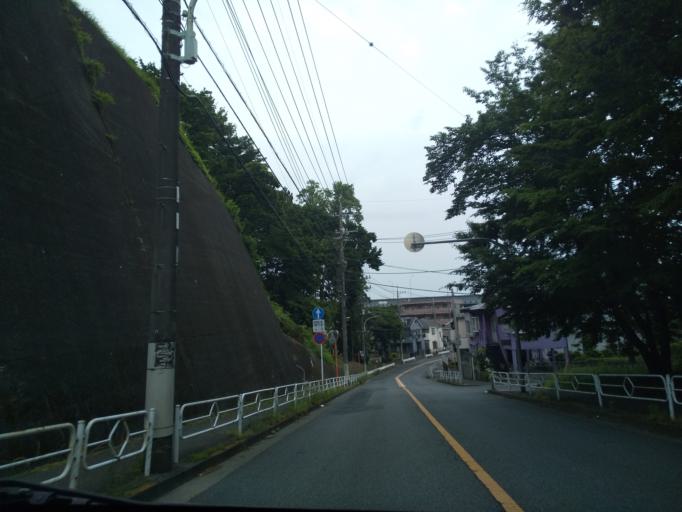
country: JP
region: Tokyo
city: Hino
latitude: 35.6734
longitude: 139.3995
